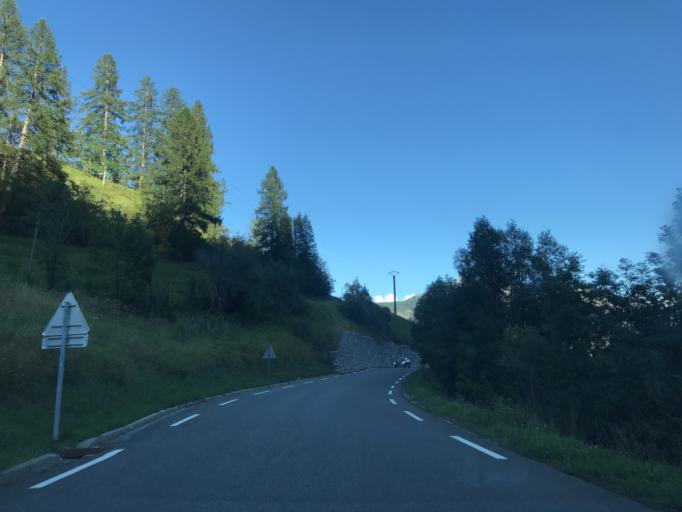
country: FR
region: Provence-Alpes-Cote d'Azur
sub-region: Departement des Hautes-Alpes
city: Guillestre
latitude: 44.7615
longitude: 6.7442
